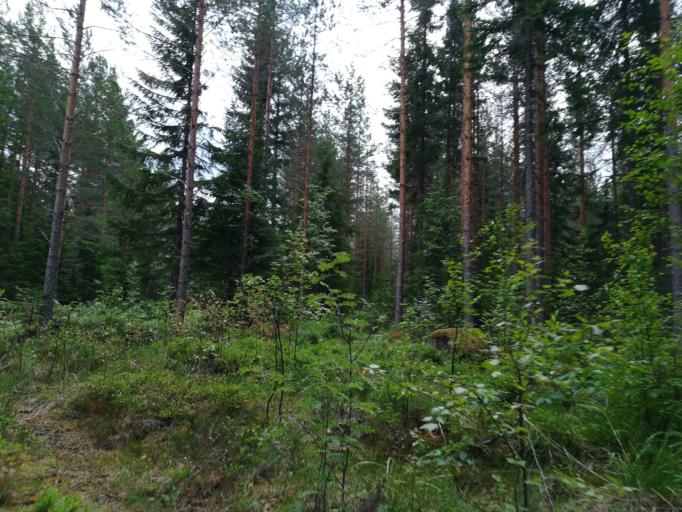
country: FI
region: South Karelia
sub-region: Lappeenranta
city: Savitaipale
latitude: 61.3029
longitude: 27.6180
